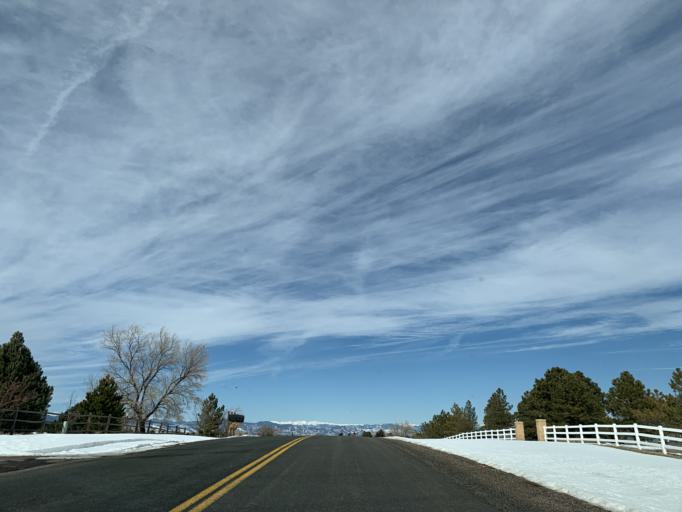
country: US
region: Colorado
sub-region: Douglas County
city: Carriage Club
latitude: 39.5162
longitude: -104.9047
